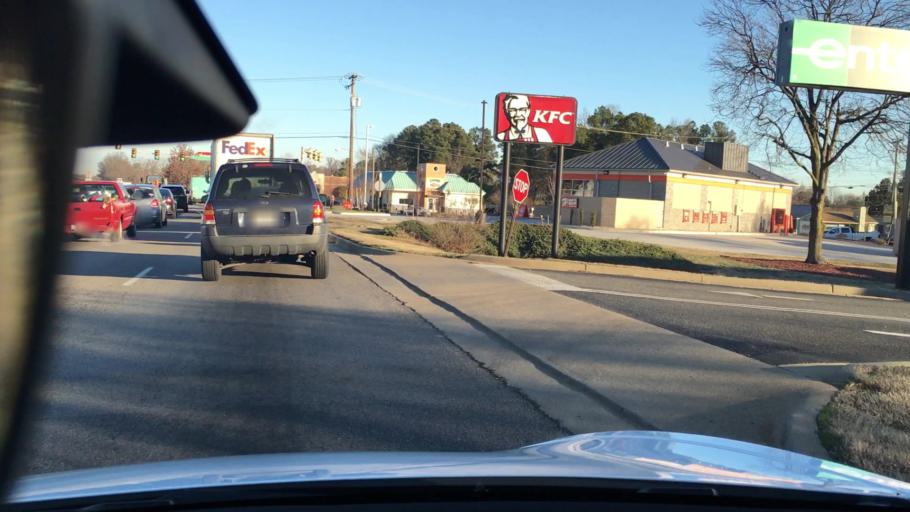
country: US
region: Virginia
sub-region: Henrico County
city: Fort Lee
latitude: 37.5162
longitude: -77.3496
